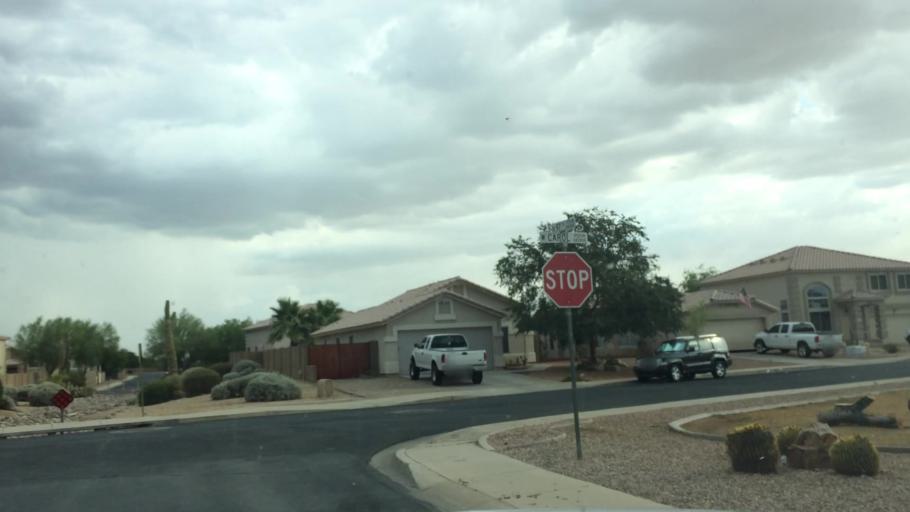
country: US
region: Arizona
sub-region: Maricopa County
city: Sun City
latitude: 33.5709
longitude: -112.2685
